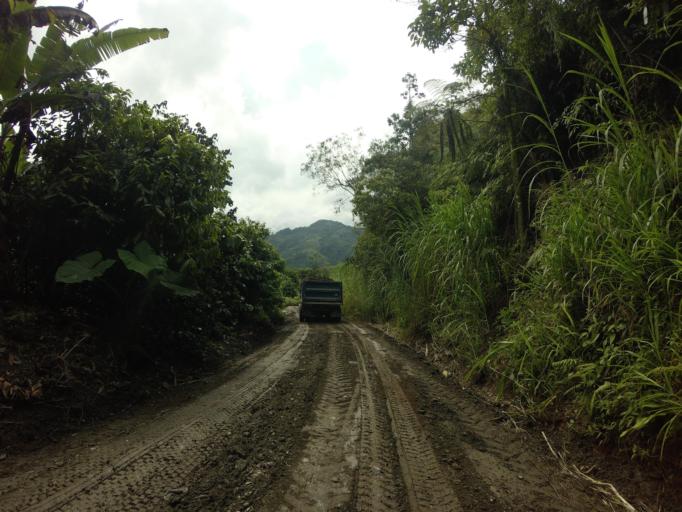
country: CO
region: Caldas
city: Marquetalia
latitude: 5.3218
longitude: -75.0448
